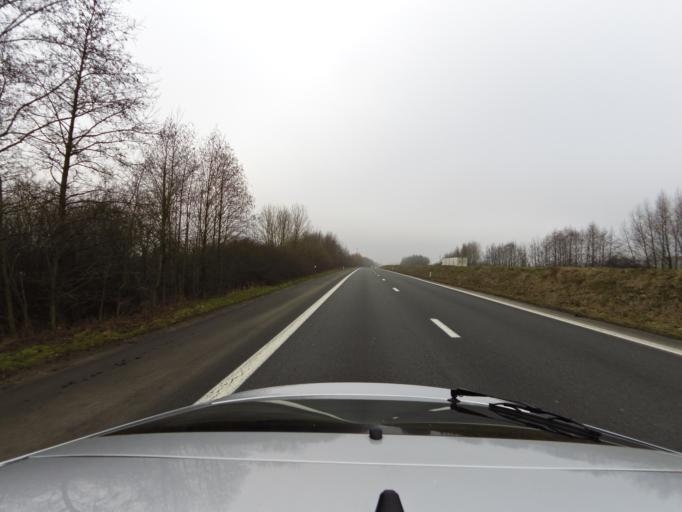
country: BE
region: Wallonia
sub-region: Province du Hainaut
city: Estaimpuis
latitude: 50.7661
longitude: 3.2776
